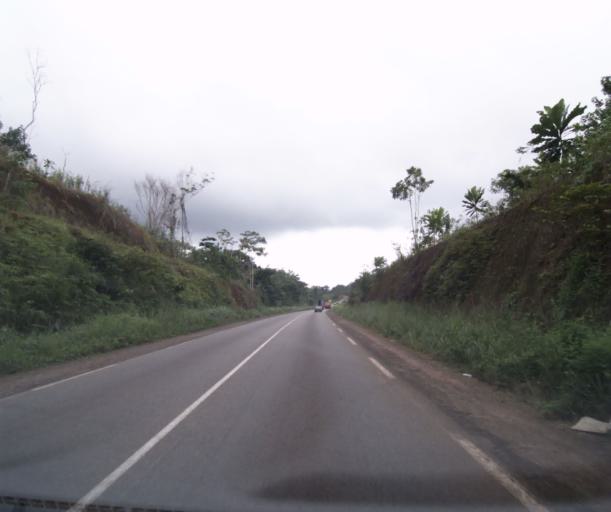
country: CM
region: Littoral
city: Edea
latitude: 3.7997
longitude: 10.2224
